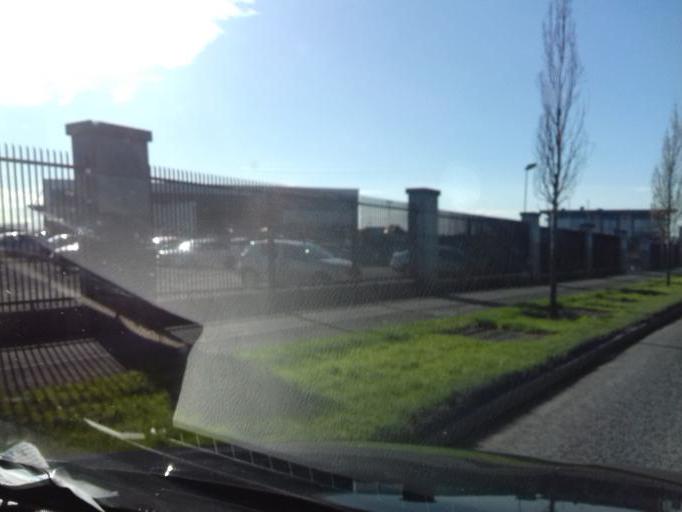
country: IE
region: Leinster
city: Castleknock
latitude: 53.4038
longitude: -6.3395
